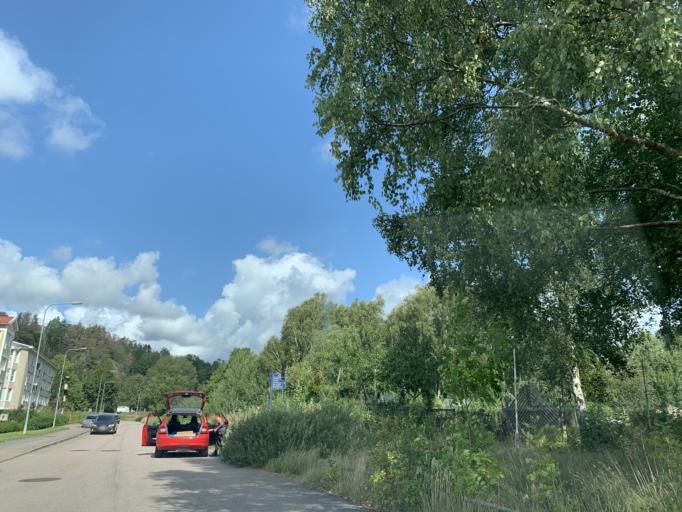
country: SE
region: Vaestra Goetaland
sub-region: Goteborg
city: Eriksbo
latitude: 57.7704
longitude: 12.0459
